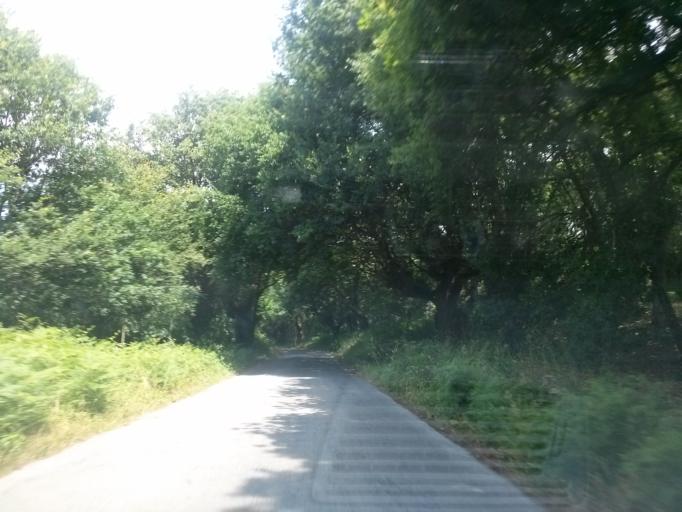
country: ES
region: Galicia
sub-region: Provincia de Lugo
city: Outeiro de Rei
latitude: 43.0421
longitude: -7.6144
